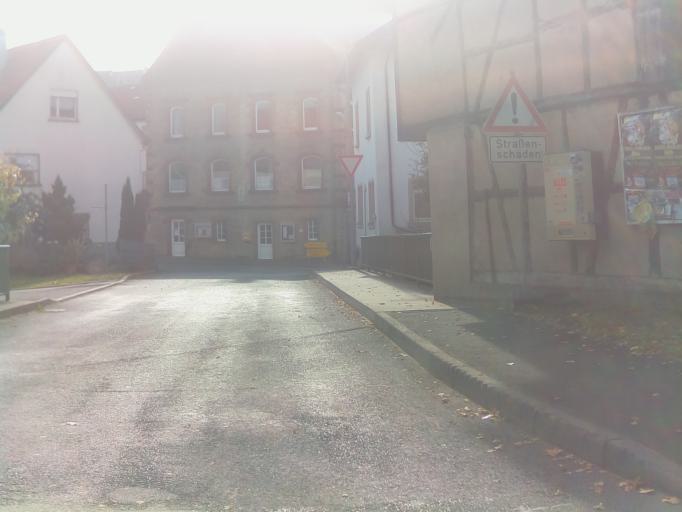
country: DE
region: Baden-Wuerttemberg
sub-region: Regierungsbezirk Stuttgart
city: Krautheim
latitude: 49.4109
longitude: 9.6120
